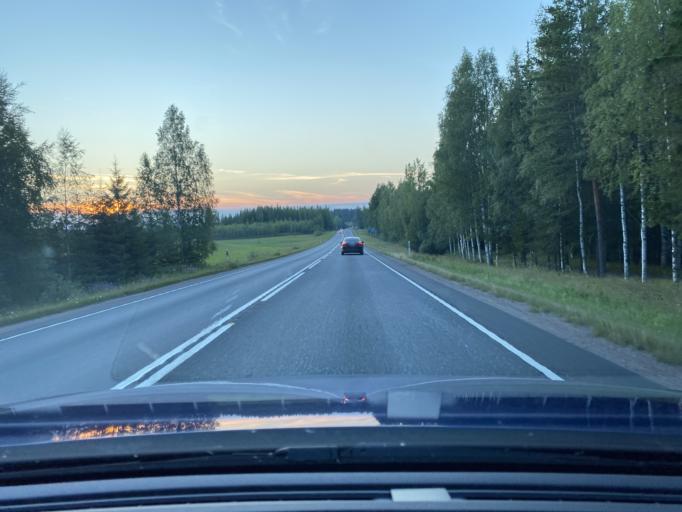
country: FI
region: Pirkanmaa
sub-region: Luoteis-Pirkanmaa
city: Ikaalinen
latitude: 61.8404
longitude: 22.9352
